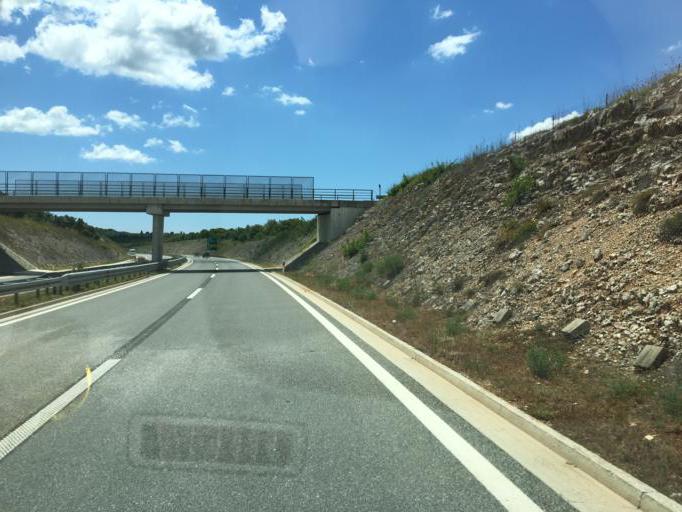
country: HR
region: Istarska
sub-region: Grad Rovinj
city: Rovinj
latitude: 45.1593
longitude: 13.7294
